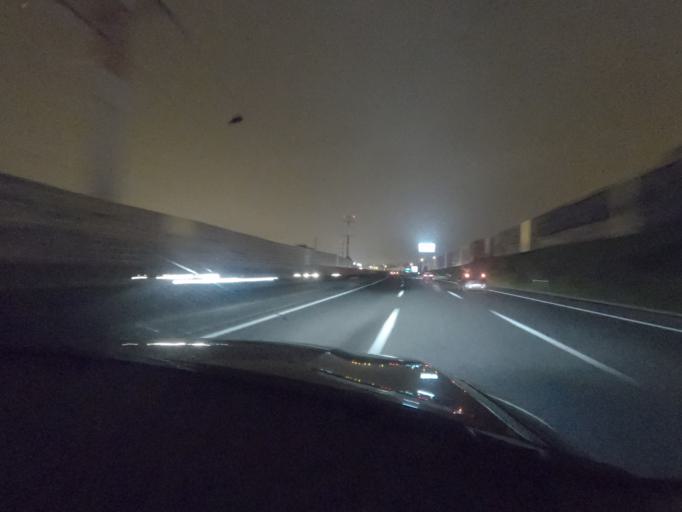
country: PT
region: Lisbon
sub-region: Loures
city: Santa Iria da Azoia
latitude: 38.8425
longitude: -9.0935
